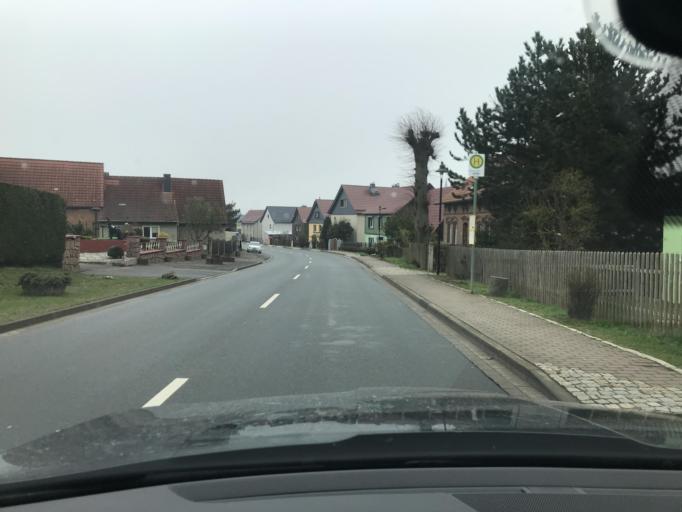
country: DE
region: Saxony-Anhalt
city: Harzgerode
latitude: 51.6034
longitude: 11.1983
